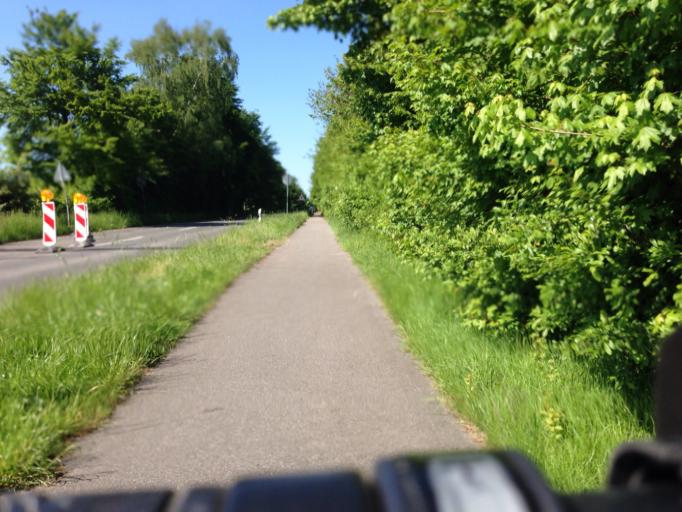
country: DE
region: Schleswig-Holstein
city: Stapelfeld
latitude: 53.6107
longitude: 10.2214
